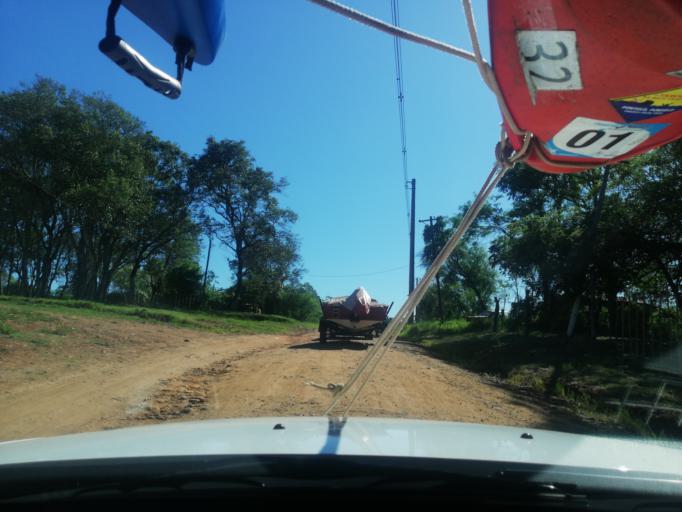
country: AR
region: Misiones
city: Santa Ana
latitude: -27.3375
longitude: -55.5847
